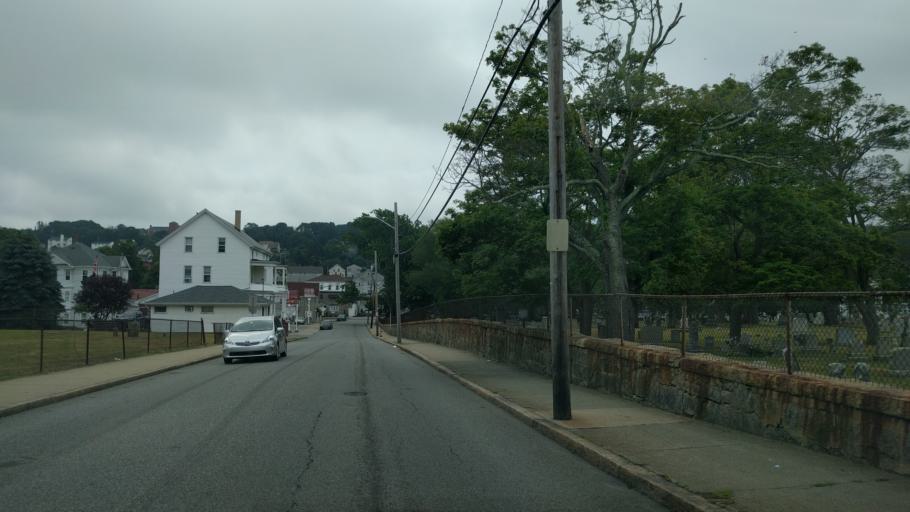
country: US
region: Massachusetts
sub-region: Bristol County
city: Fall River
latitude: 41.7213
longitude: -71.1483
